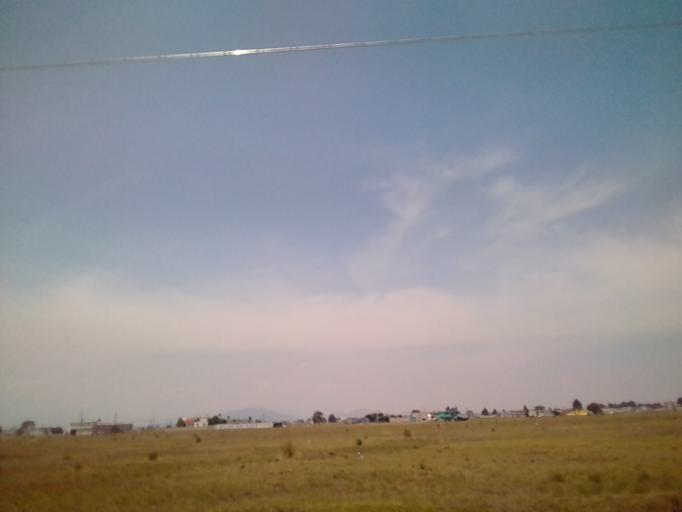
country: MX
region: Mexico
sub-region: Toluca
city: Guadalupe Totoltepec
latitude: 19.3566
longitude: -99.5602
